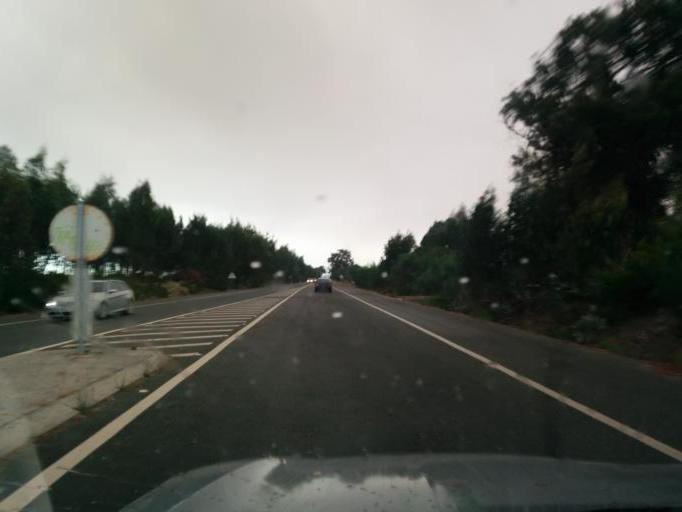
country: PT
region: Beja
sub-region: Odemira
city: Vila Nova de Milfontes
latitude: 37.7044
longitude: -8.7706
